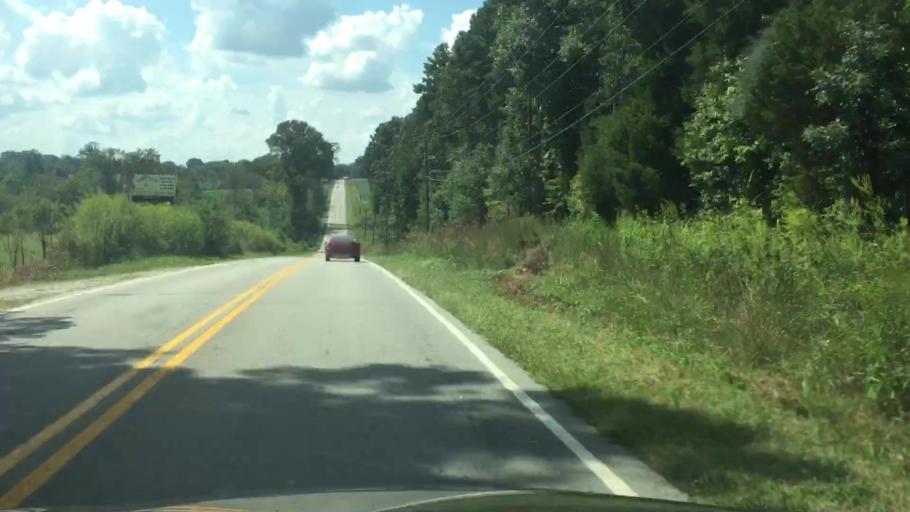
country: US
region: North Carolina
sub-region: Rowan County
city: China Grove
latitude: 35.6496
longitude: -80.6148
